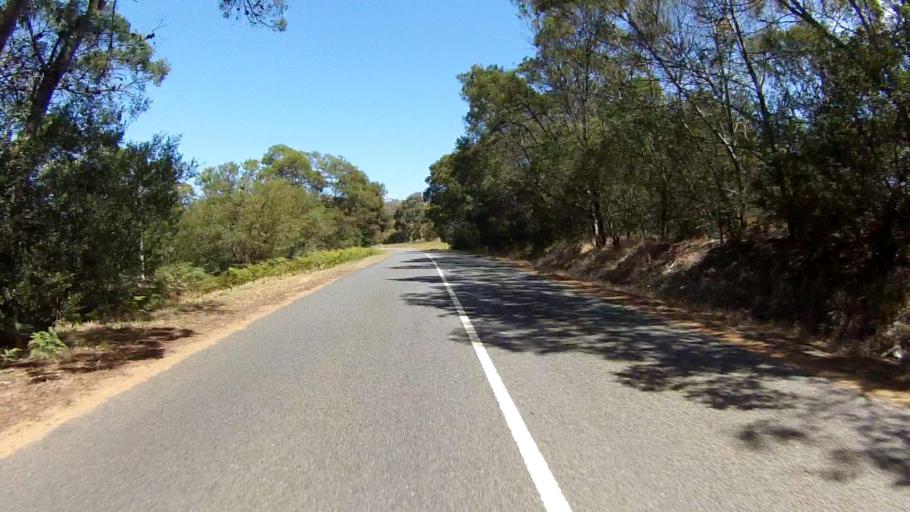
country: AU
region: Tasmania
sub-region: Clarence
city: Sandford
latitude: -42.9923
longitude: 147.4777
